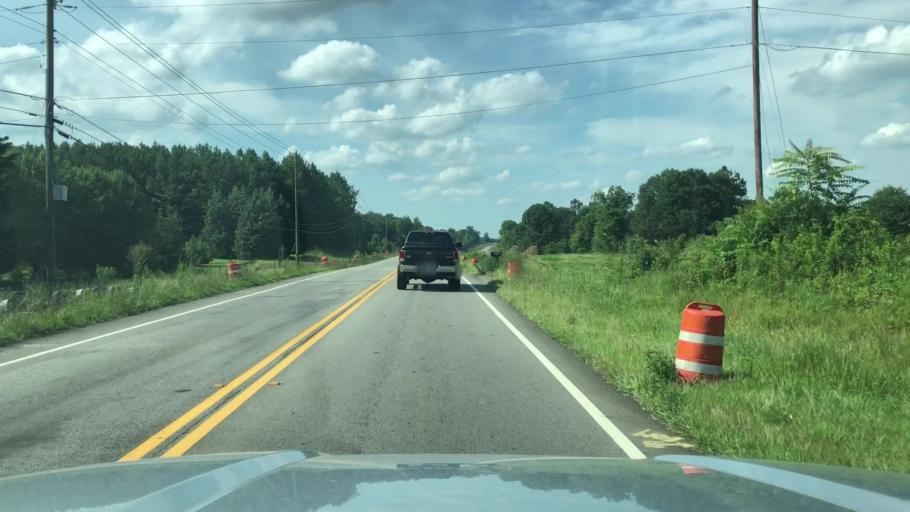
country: US
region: Georgia
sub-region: Paulding County
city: Hiram
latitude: 33.8247
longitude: -84.7591
